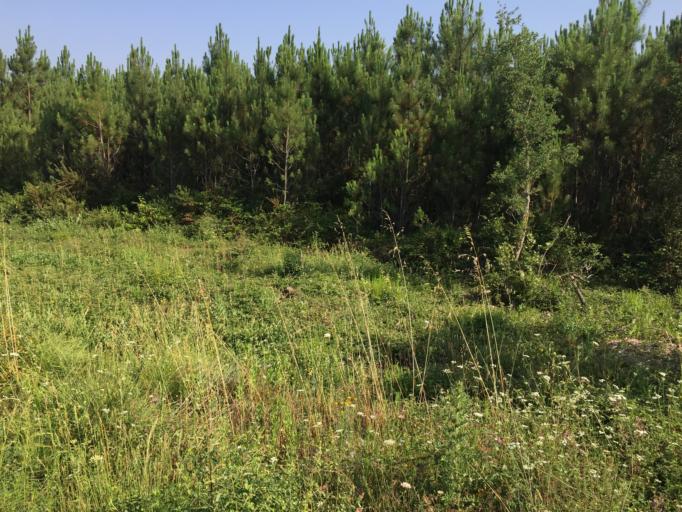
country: PT
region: Coimbra
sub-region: Cantanhede
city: Cantanhede
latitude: 40.4205
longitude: -8.5432
